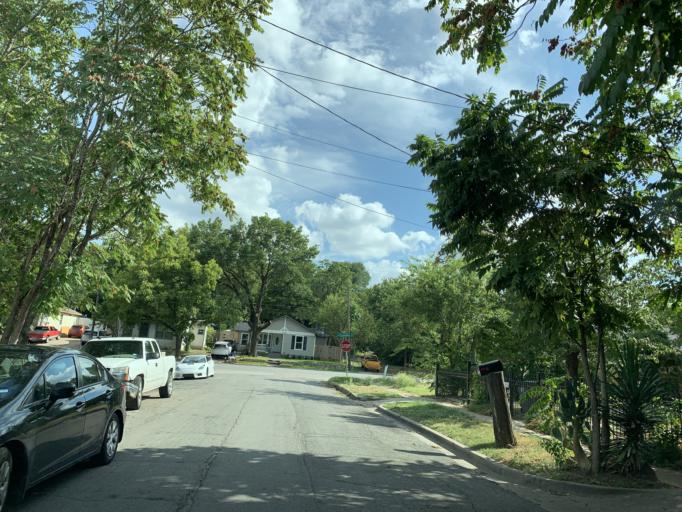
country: US
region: Texas
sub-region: Dallas County
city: Cockrell Hill
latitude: 32.7359
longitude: -96.8418
